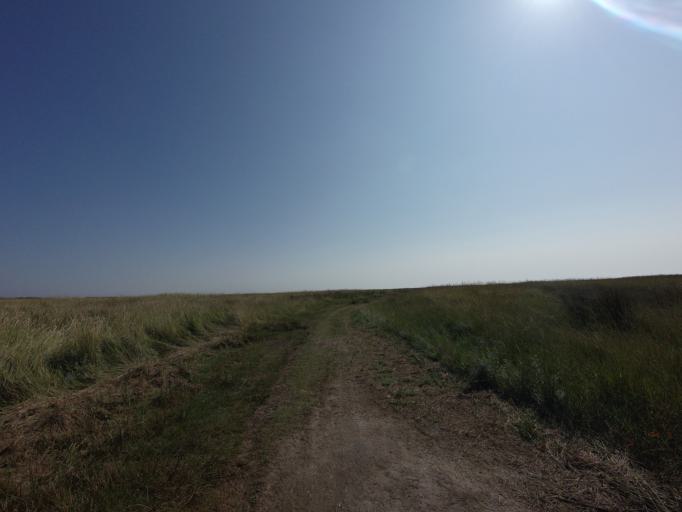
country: NL
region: Friesland
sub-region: Gemeente Schiermonnikoog
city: Schiermonnikoog
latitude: 53.4903
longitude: 6.2278
